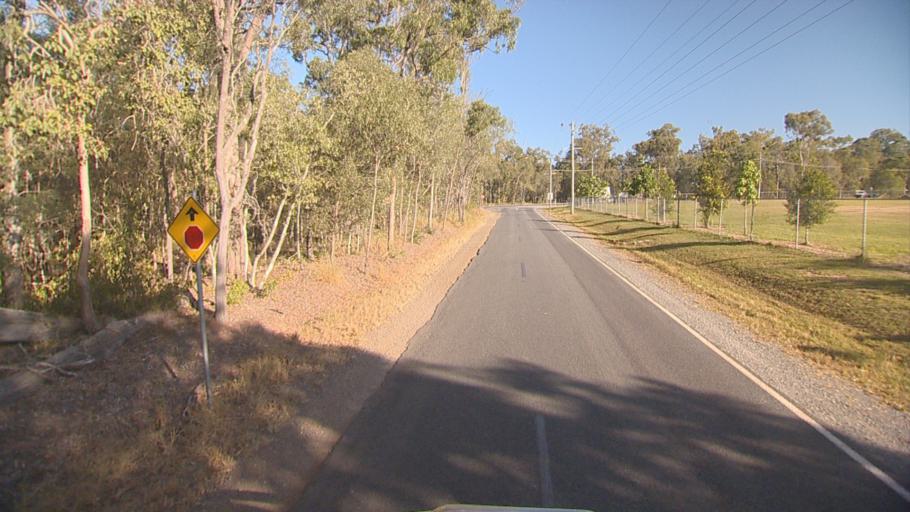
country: AU
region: Queensland
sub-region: Logan
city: North Maclean
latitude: -27.7902
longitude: 153.0381
